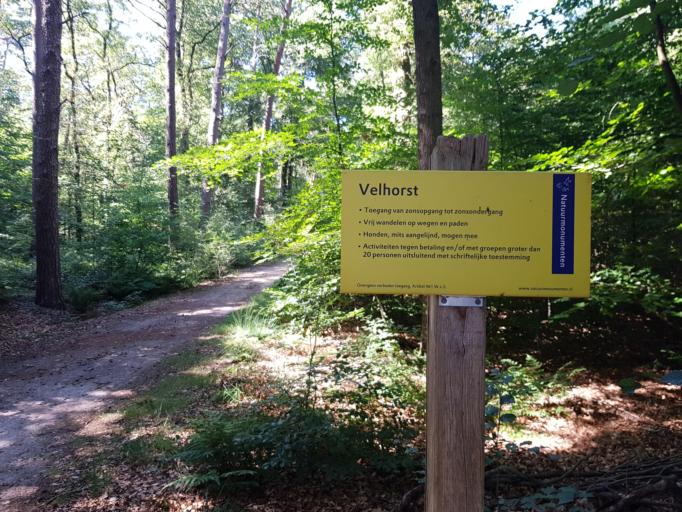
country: NL
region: Gelderland
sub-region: Gemeente Lochem
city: Almen
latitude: 52.1499
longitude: 6.3435
